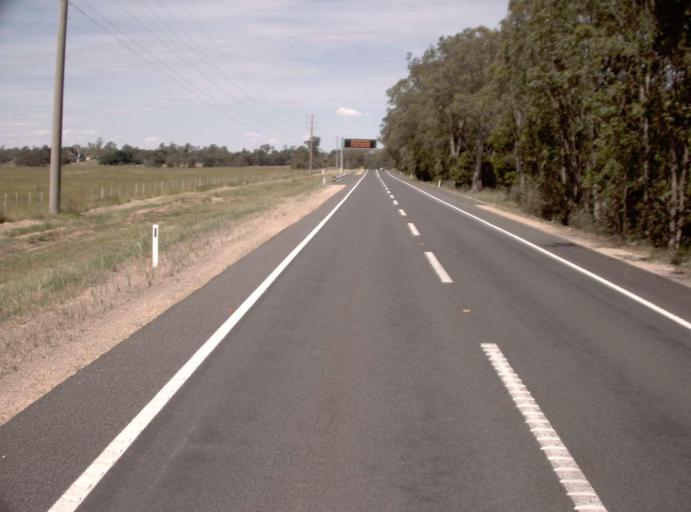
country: AU
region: Victoria
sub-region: East Gippsland
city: Bairnsdale
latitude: -37.9023
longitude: 147.3481
